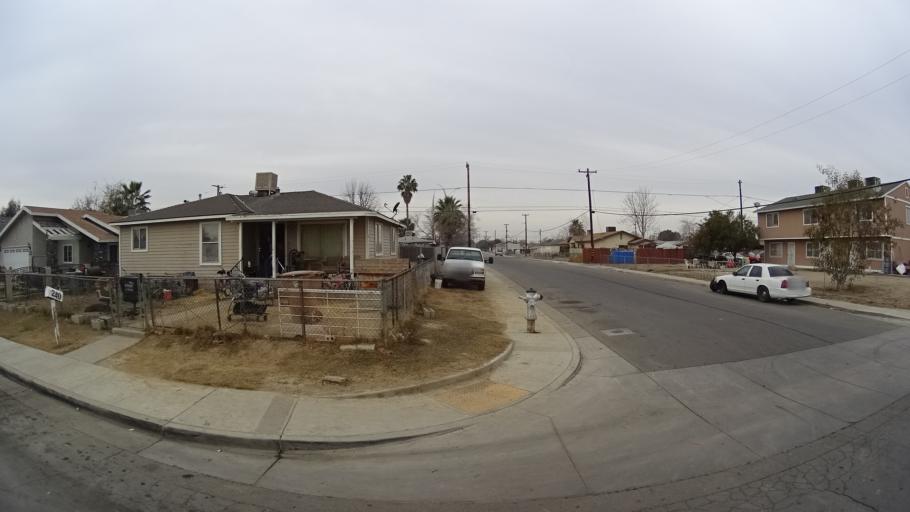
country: US
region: California
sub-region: Kern County
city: Bakersfield
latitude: 35.3593
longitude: -118.9864
